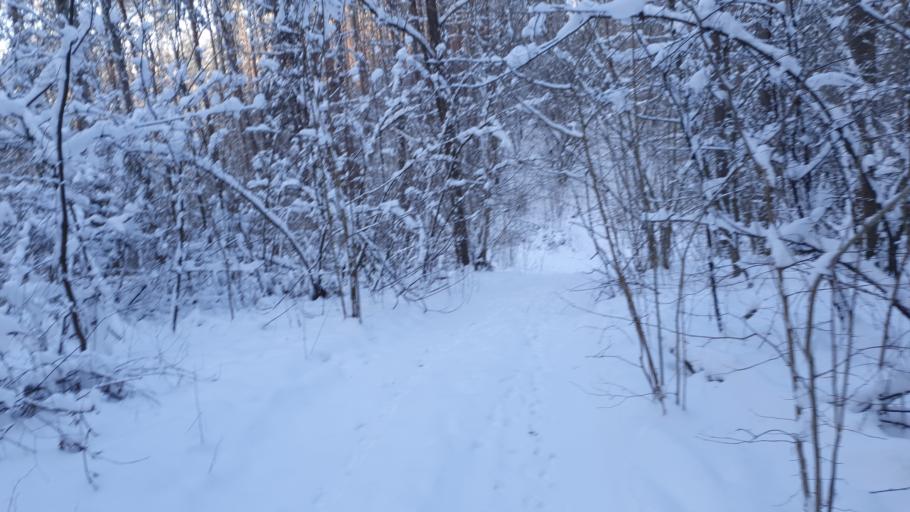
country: LT
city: Skaidiskes
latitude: 54.6451
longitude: 25.4186
